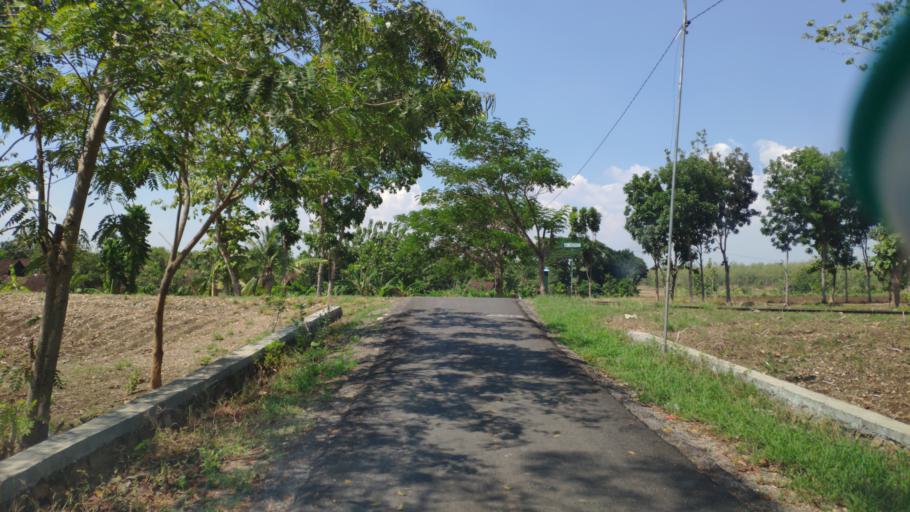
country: ID
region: Central Java
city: Galuk
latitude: -7.0874
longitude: 111.5030
